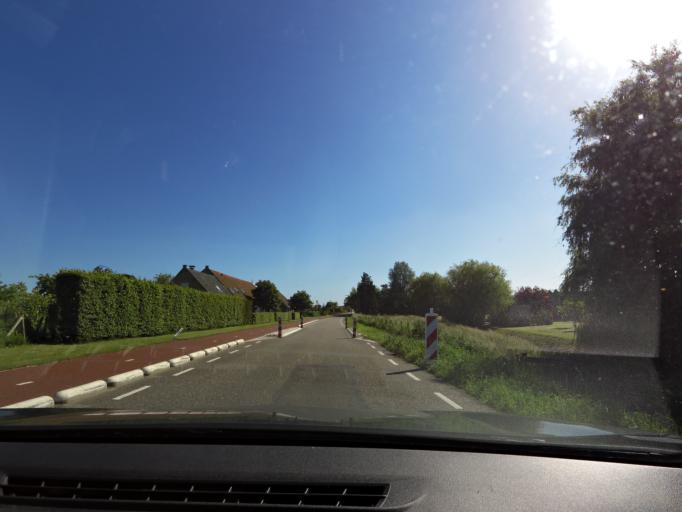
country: NL
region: South Holland
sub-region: Gemeente Brielle
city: Brielle
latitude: 51.8748
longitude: 4.1751
